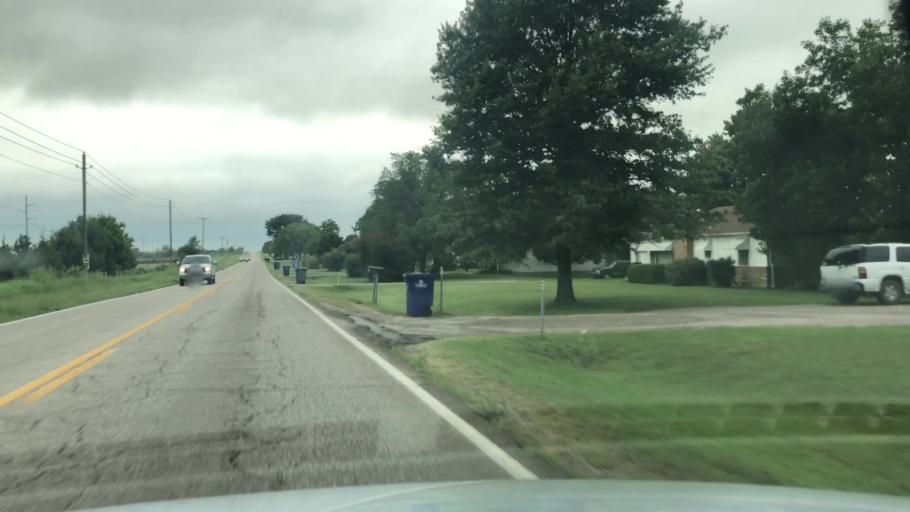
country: US
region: Oklahoma
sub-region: Nowata County
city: Nowata
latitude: 36.7045
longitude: -95.6507
